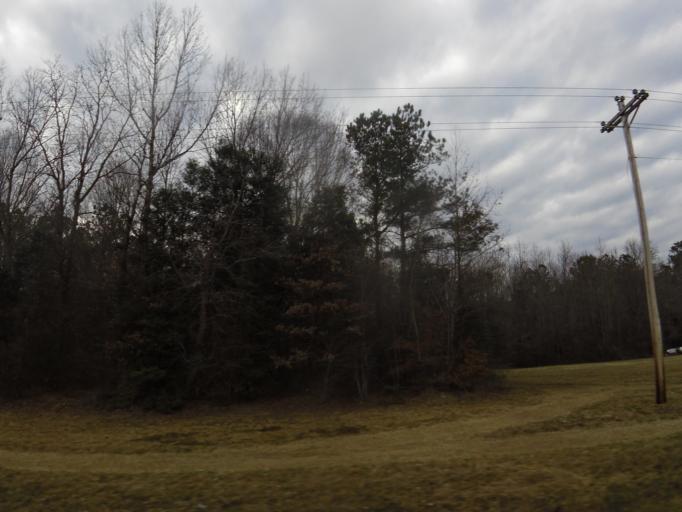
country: US
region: North Carolina
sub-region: Hertford County
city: Murfreesboro
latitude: 36.3888
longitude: -77.1580
